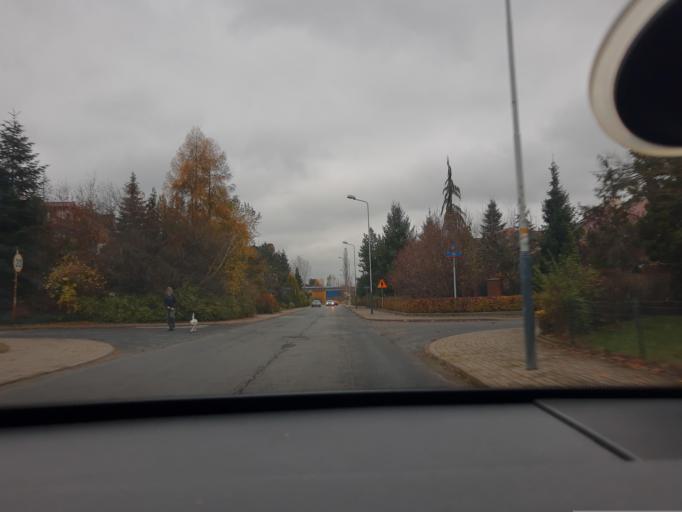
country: PL
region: Lodz Voivodeship
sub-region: Powiat pabianicki
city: Konstantynow Lodzki
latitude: 51.7365
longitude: 19.3758
